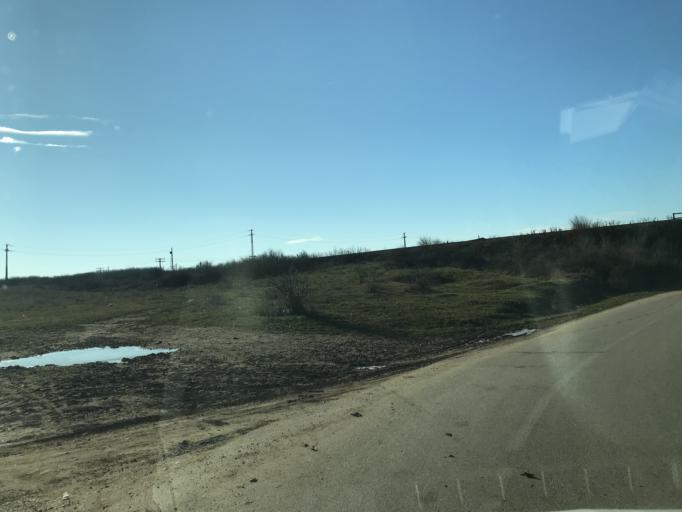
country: RO
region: Olt
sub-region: Comuna Piatra Olt
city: Piatra Olt
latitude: 44.3585
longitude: 24.2521
